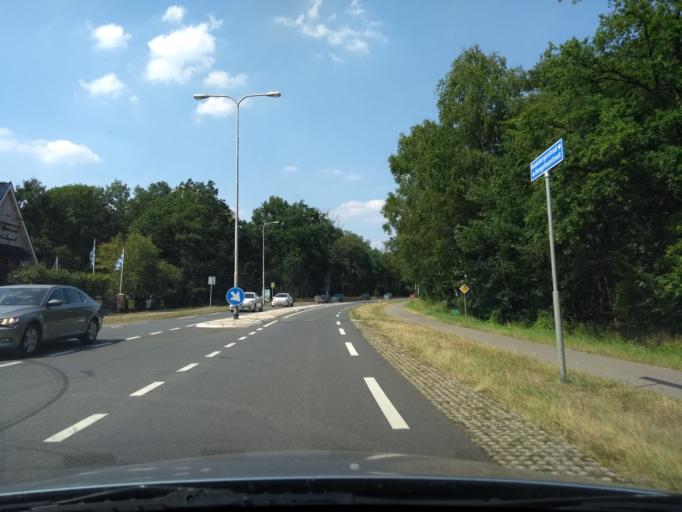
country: NL
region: Overijssel
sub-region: Gemeente Haaksbergen
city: Haaksbergen
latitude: 52.2010
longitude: 6.7306
